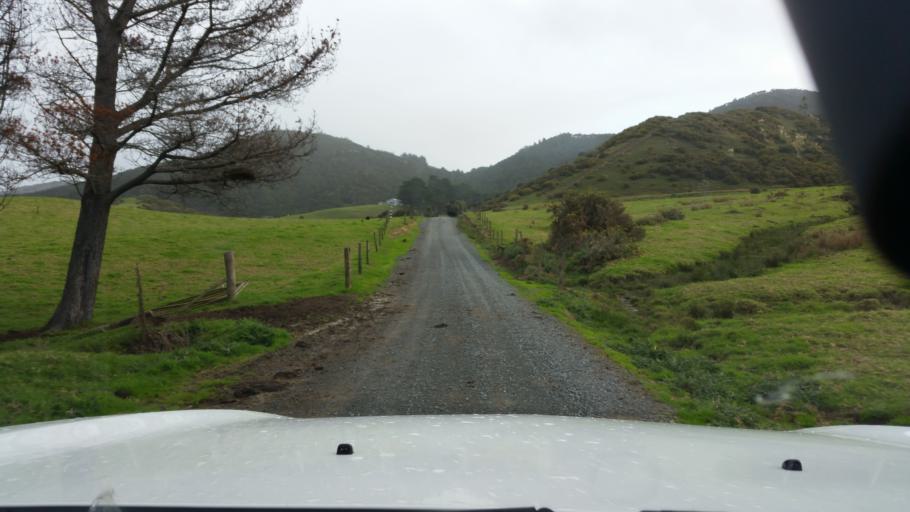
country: NZ
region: Northland
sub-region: Whangarei
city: Ruakaka
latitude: -35.7815
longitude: 174.5481
